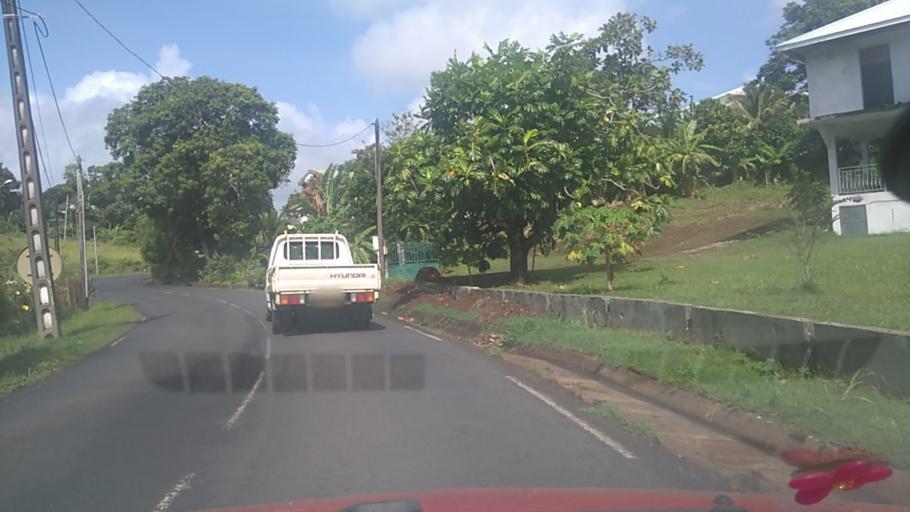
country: MQ
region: Martinique
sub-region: Martinique
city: Le Francois
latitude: 14.5974
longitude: -60.9276
